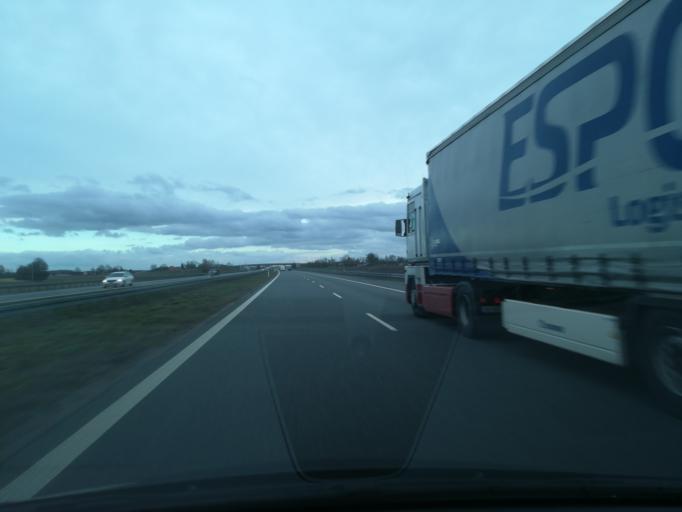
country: PL
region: Lodz Voivodeship
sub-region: Powiat kutnowski
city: Lanieta
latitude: 52.4083
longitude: 19.2704
